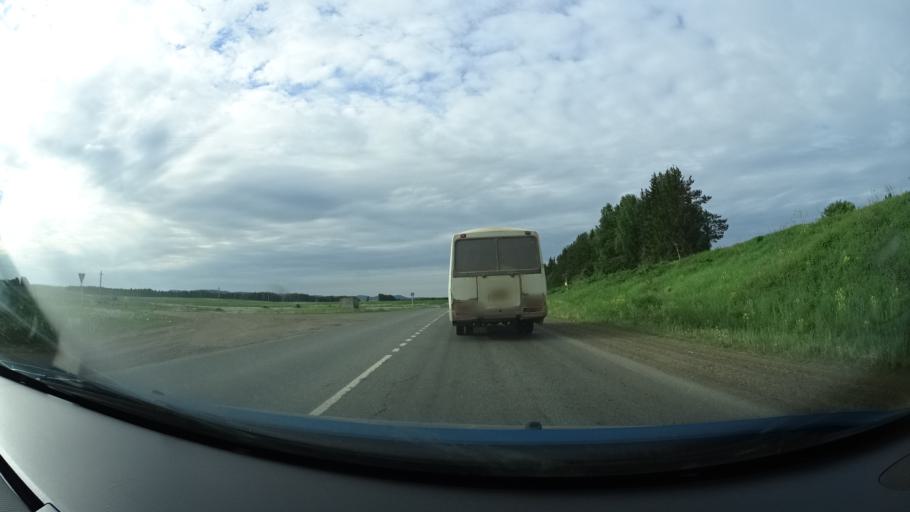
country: RU
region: Perm
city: Osa
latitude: 57.2683
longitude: 55.5722
